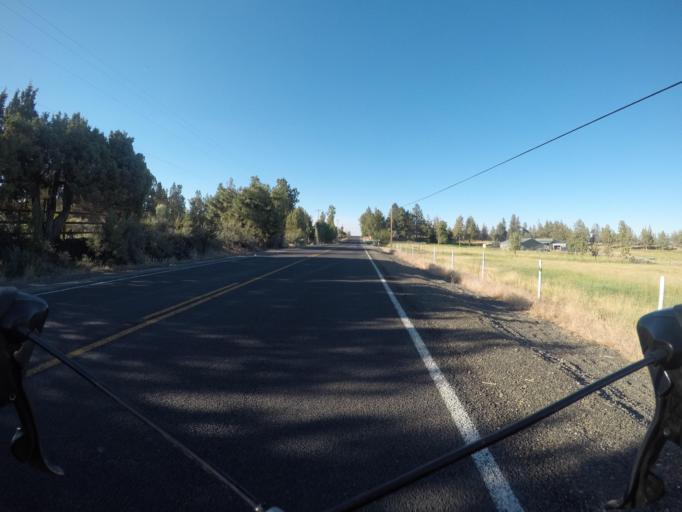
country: US
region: Oregon
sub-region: Deschutes County
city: Redmond
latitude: 44.2564
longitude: -121.2396
